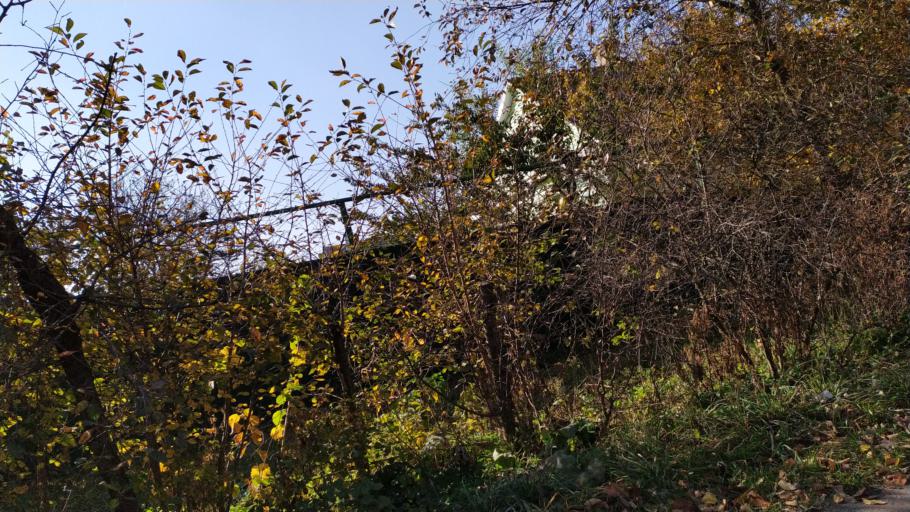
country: RU
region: Kursk
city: Kursk
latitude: 51.6468
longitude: 36.1503
